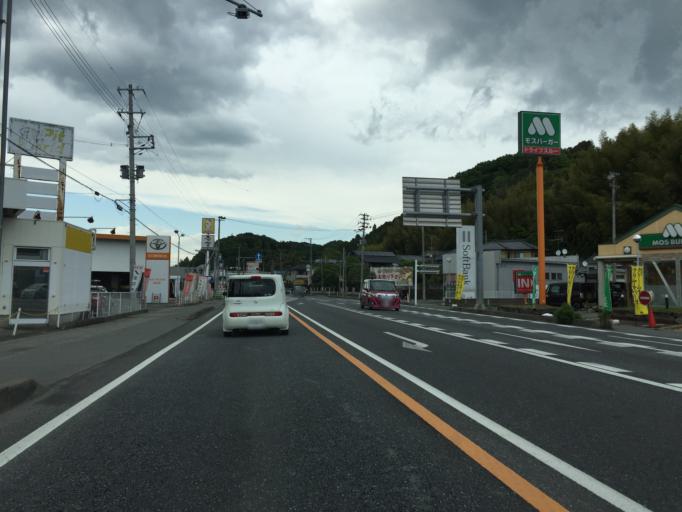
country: JP
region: Fukushima
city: Iwaki
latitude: 36.9874
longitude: 140.8687
